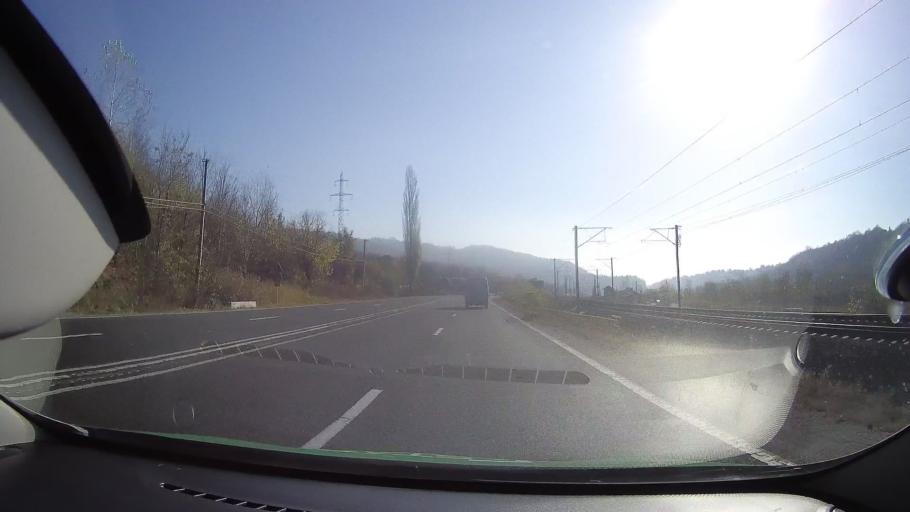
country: RO
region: Prahova
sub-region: Oras Breaza
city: Breaza
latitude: 45.1961
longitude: 25.6705
